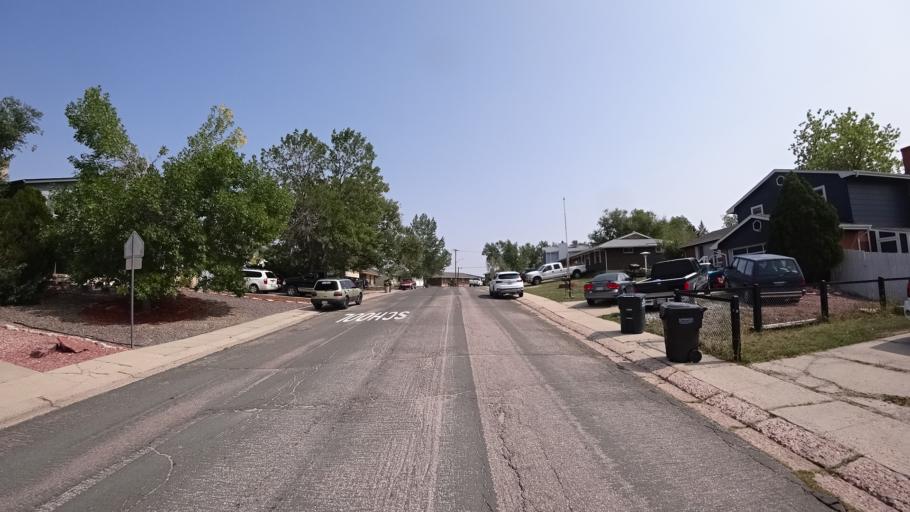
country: US
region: Colorado
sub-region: El Paso County
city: Stratmoor
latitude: 38.8092
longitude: -104.7706
